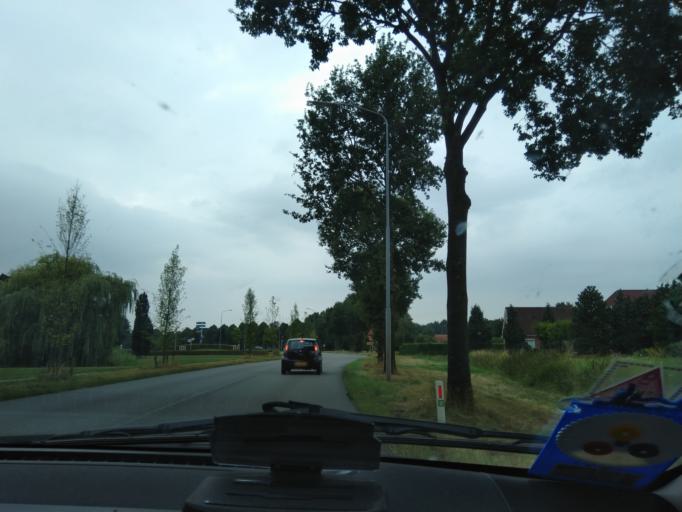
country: NL
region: Groningen
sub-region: Gemeente Pekela
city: Oude Pekela
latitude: 53.1137
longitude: 7.0233
